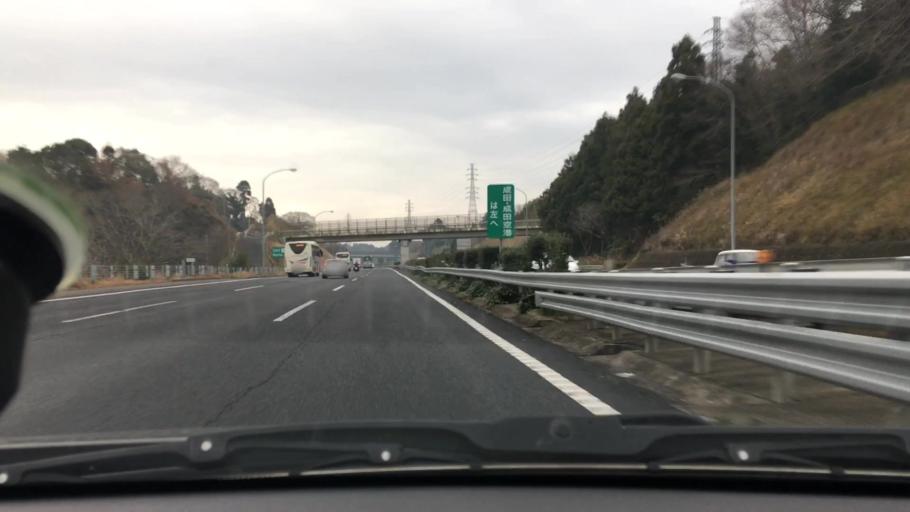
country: JP
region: Chiba
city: Narita
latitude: 35.7685
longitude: 140.3309
